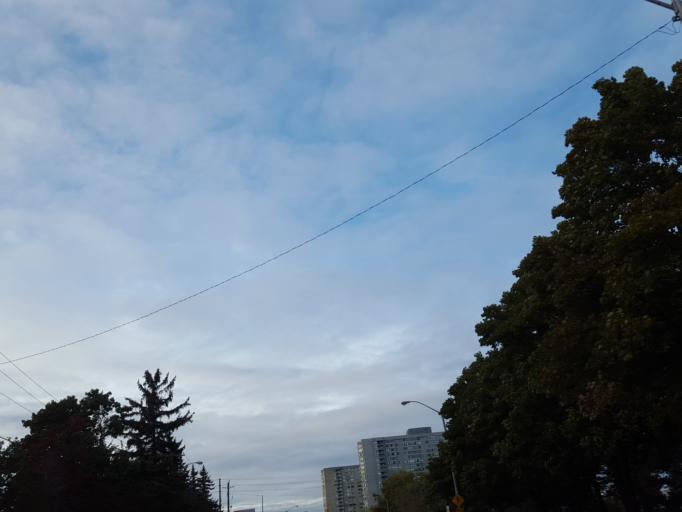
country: CA
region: Ontario
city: Scarborough
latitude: 43.7956
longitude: -79.3153
